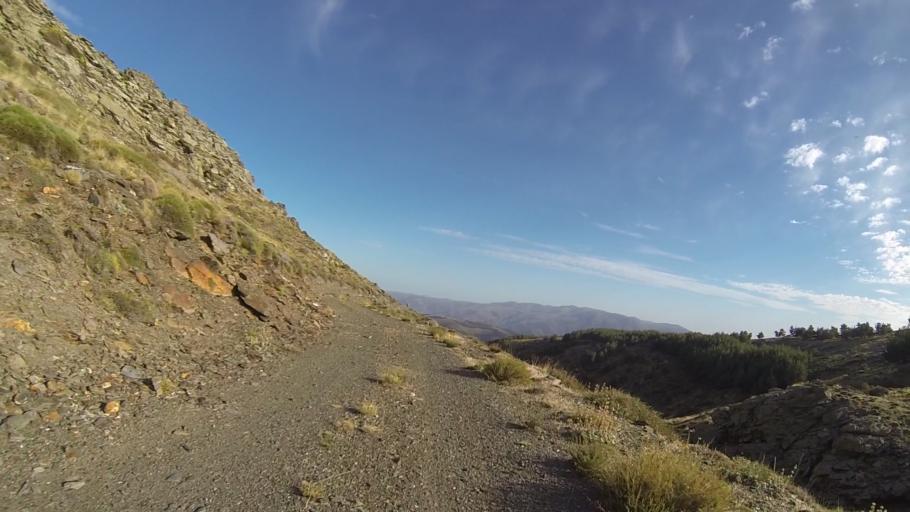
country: ES
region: Andalusia
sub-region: Provincia de Almeria
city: Paterna del Rio
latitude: 37.0768
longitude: -2.8996
